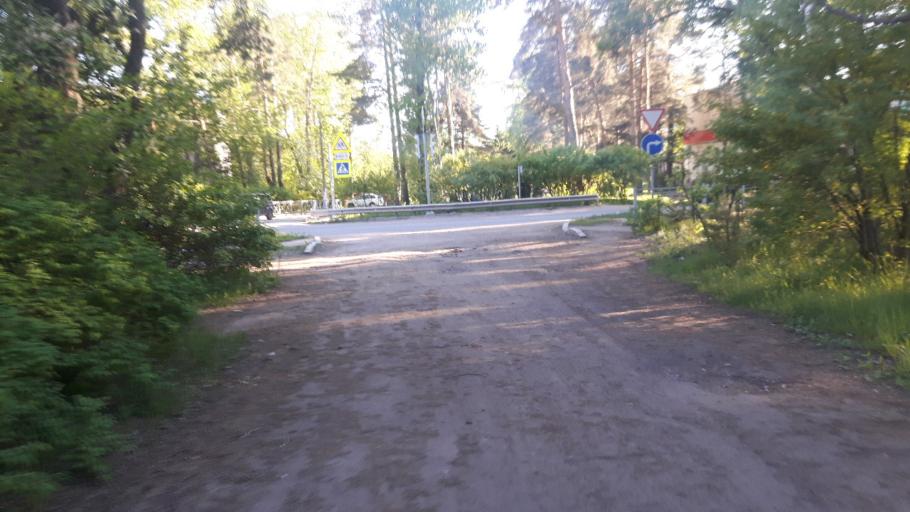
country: RU
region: St.-Petersburg
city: Bol'shaya Izhora
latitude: 59.9457
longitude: 29.5683
